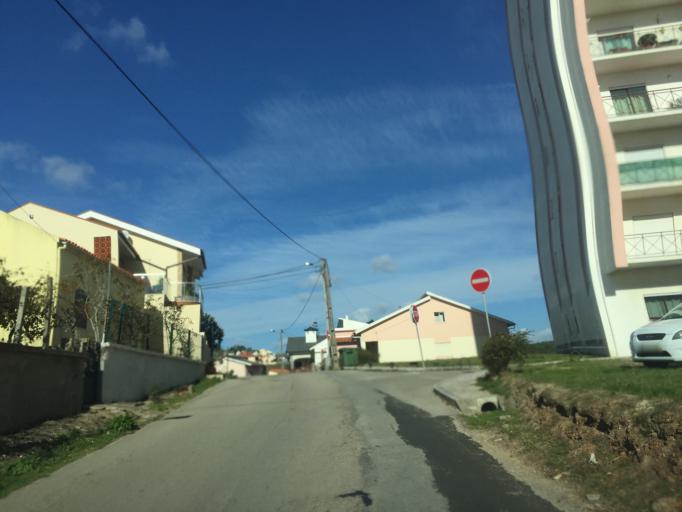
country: PT
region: Coimbra
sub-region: Figueira da Foz
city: Tavarede
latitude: 40.1684
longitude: -8.8415
